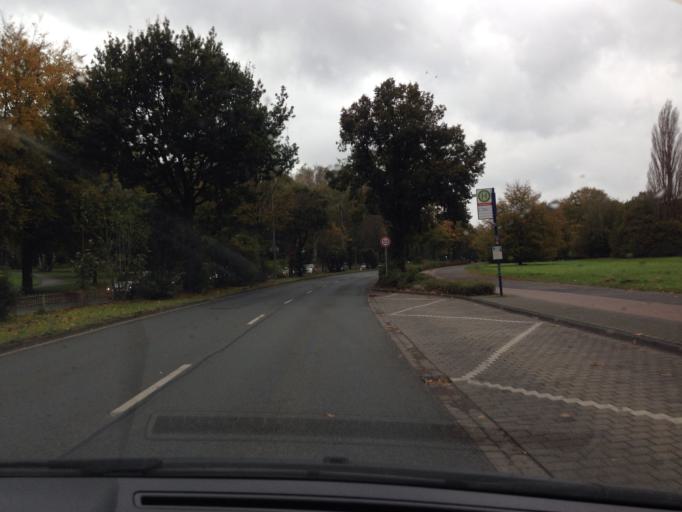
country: DE
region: North Rhine-Westphalia
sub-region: Regierungsbezirk Munster
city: Muenster
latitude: 51.9511
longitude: 7.6044
